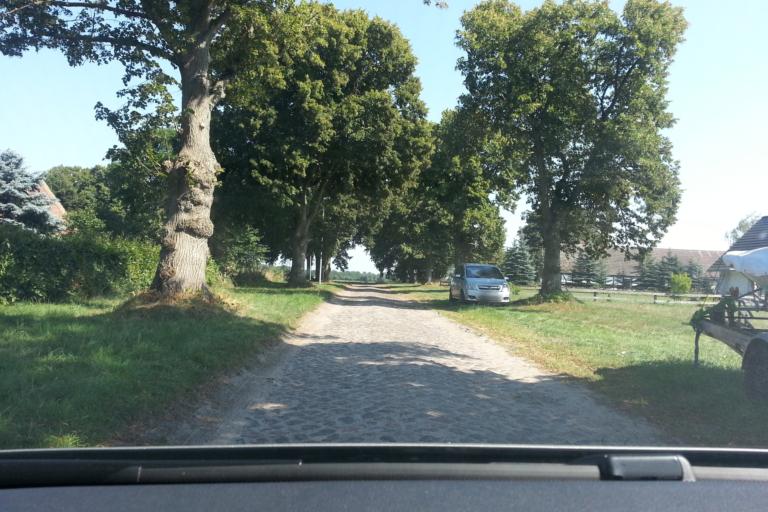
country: DE
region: Mecklenburg-Vorpommern
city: Ducherow
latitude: 53.7098
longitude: 13.7837
